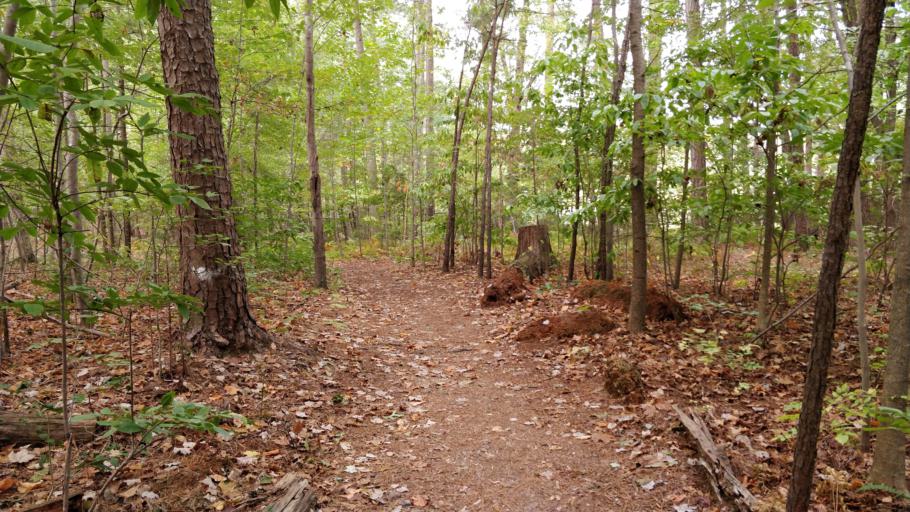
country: US
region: North Carolina
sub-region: Wake County
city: West Raleigh
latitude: 35.9089
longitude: -78.6696
